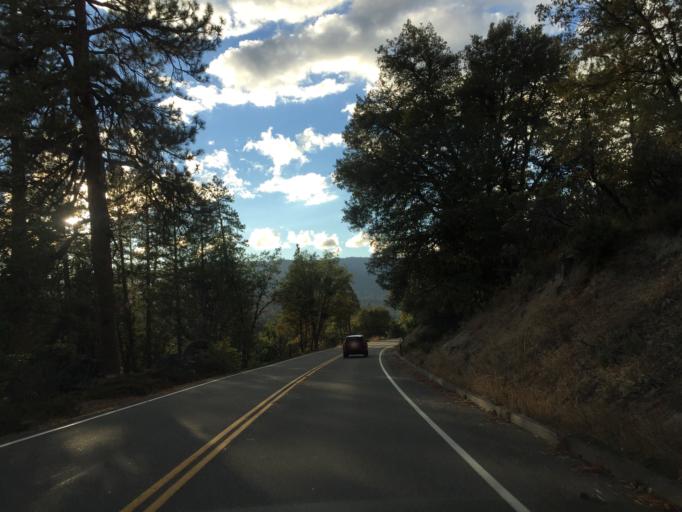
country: US
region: California
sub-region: Madera County
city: Ahwahnee
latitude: 37.5300
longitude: -119.6358
